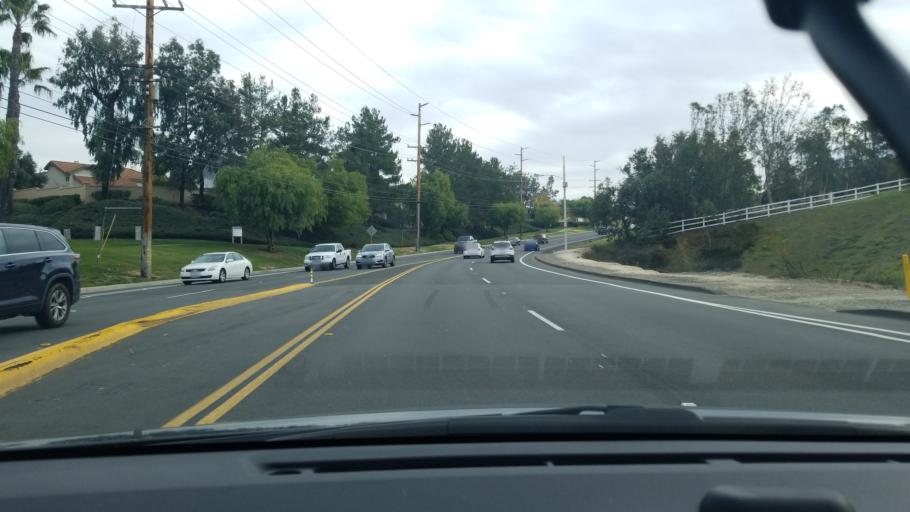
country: US
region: California
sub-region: Riverside County
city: Temecula
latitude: 33.4971
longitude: -117.1144
